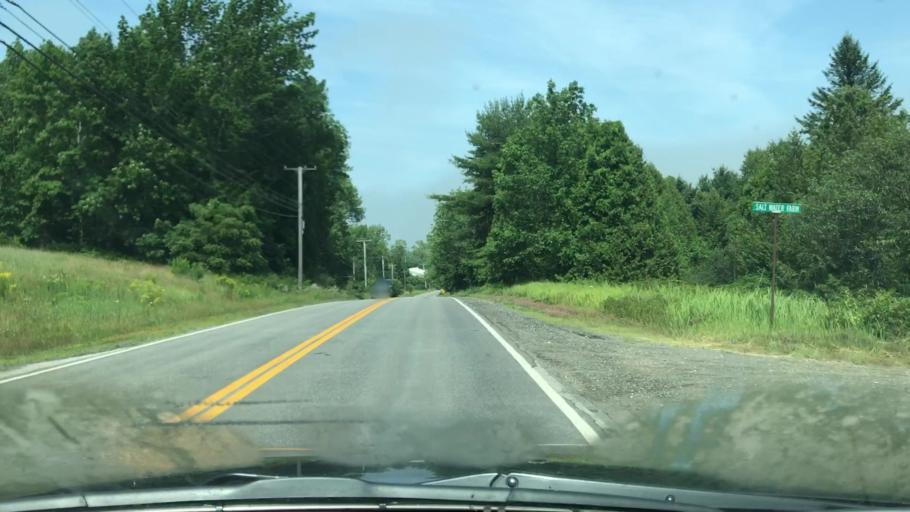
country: US
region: Maine
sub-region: Waldo County
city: Lincolnville
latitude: 44.2685
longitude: -69.0166
